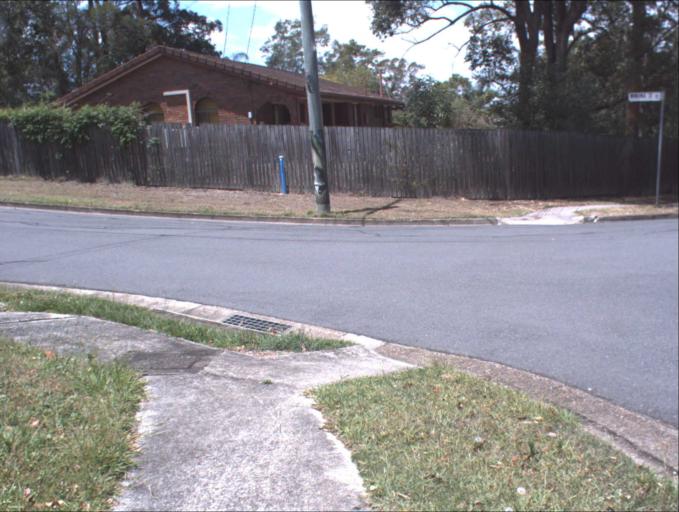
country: AU
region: Queensland
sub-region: Logan
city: Slacks Creek
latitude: -27.6392
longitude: 153.1650
